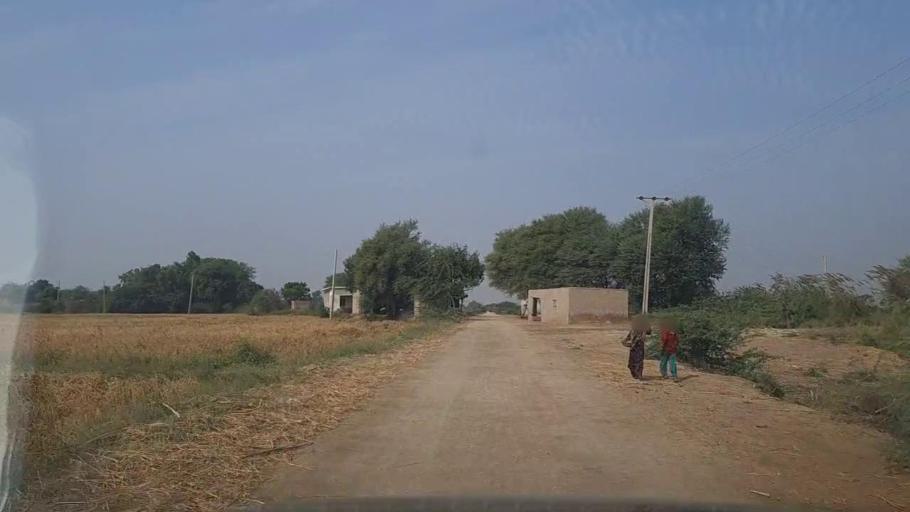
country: PK
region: Sindh
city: Bulri
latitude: 24.9776
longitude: 68.2995
